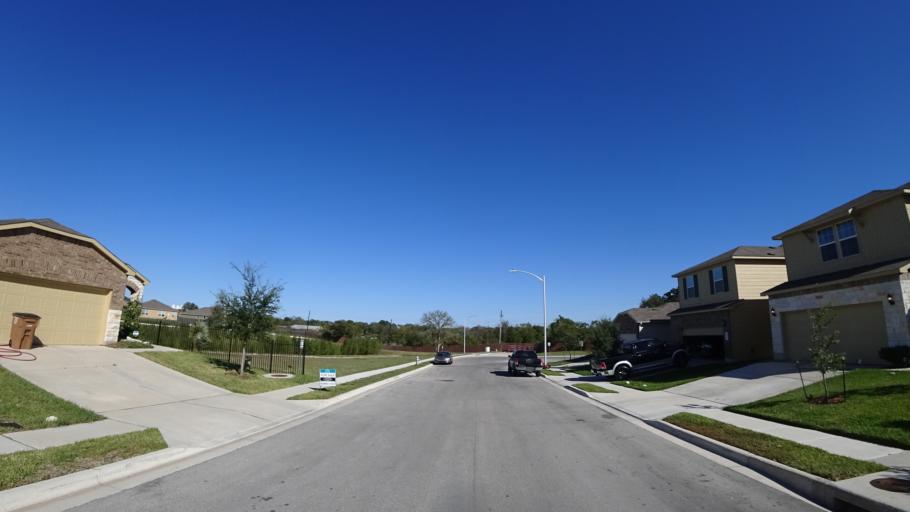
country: US
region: Texas
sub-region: Travis County
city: Hornsby Bend
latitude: 30.2772
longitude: -97.6244
